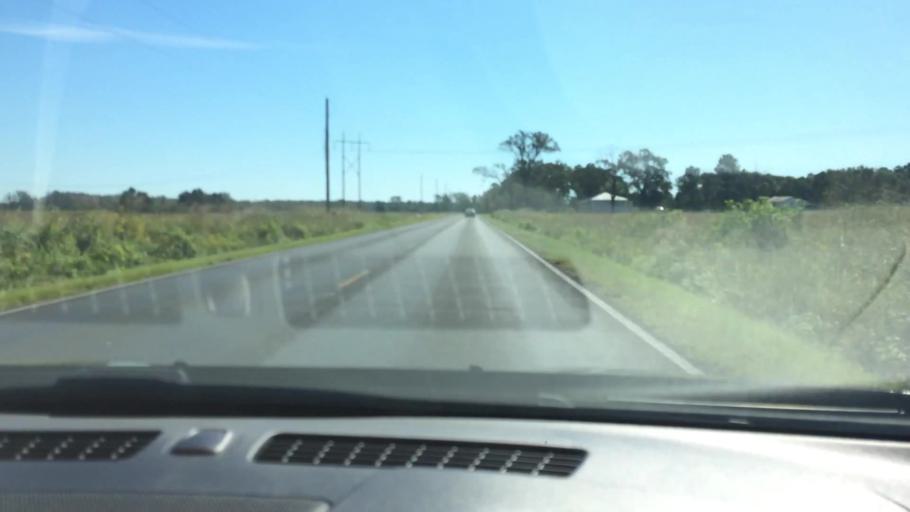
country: US
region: North Carolina
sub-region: Pitt County
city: Grifton
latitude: 35.3718
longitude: -77.3562
